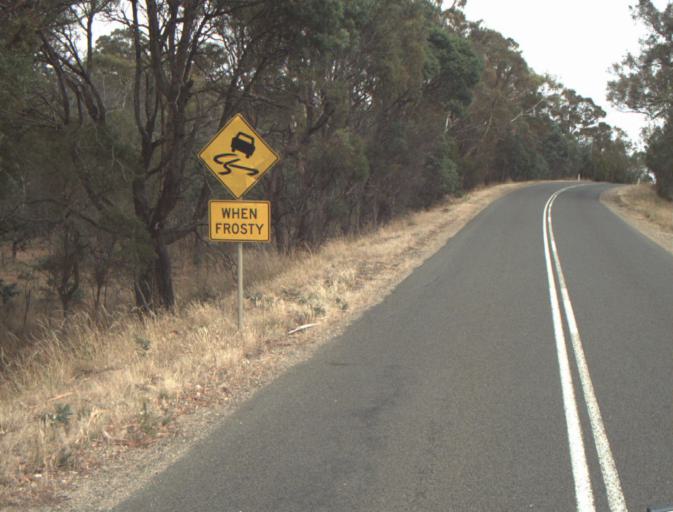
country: AU
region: Tasmania
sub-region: Northern Midlands
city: Evandale
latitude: -41.5069
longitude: 147.3577
